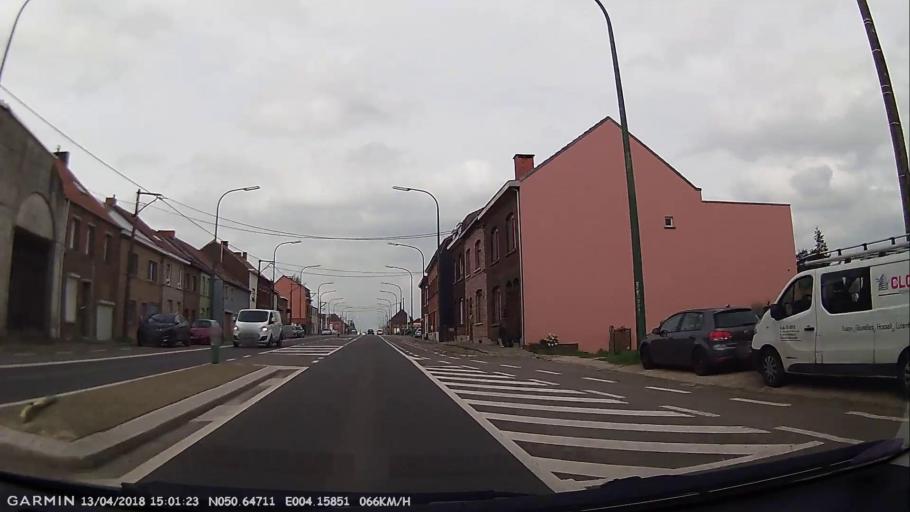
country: BE
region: Wallonia
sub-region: Province du Hainaut
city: Braine-le-Comte
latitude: 50.6472
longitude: 4.1586
